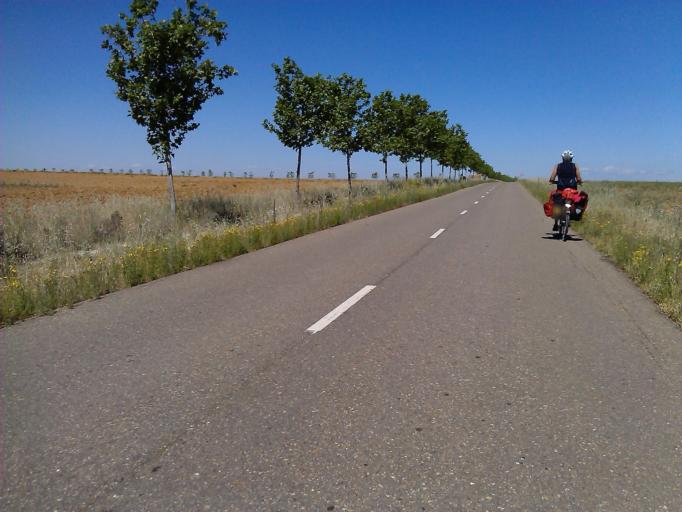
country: ES
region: Castille and Leon
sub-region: Provincia de Leon
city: Villamoratiel de las Matas
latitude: 42.4593
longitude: -5.2961
